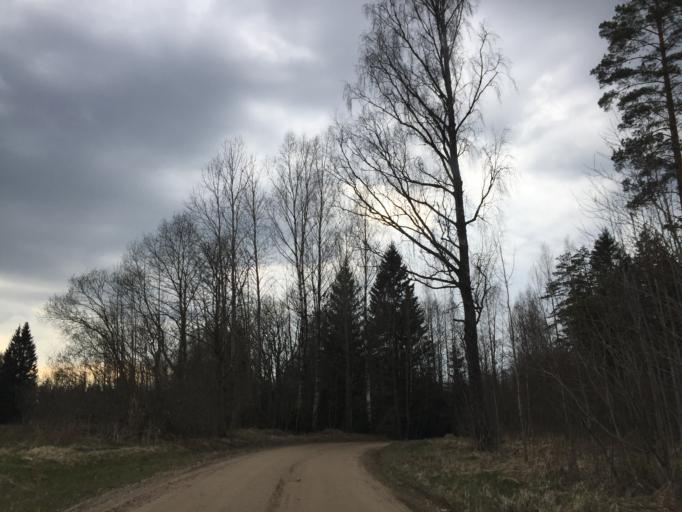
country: EE
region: Vorumaa
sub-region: Antsla vald
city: Vana-Antsla
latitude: 57.9420
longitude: 26.7231
